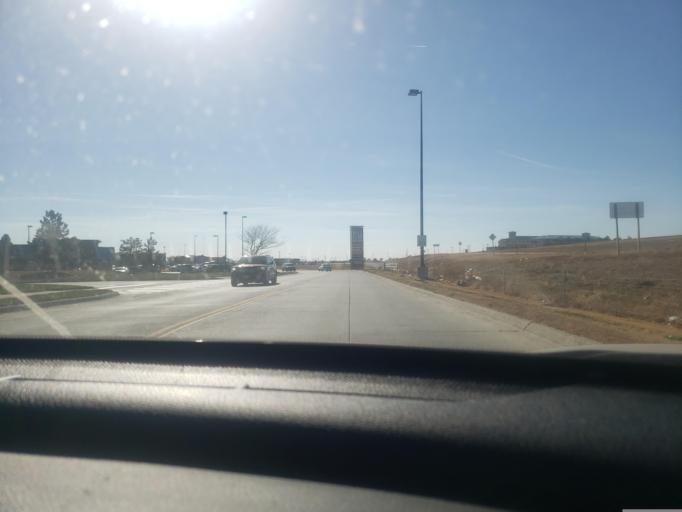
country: US
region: Kansas
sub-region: Finney County
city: Garden City
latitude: 37.9818
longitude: -100.8363
